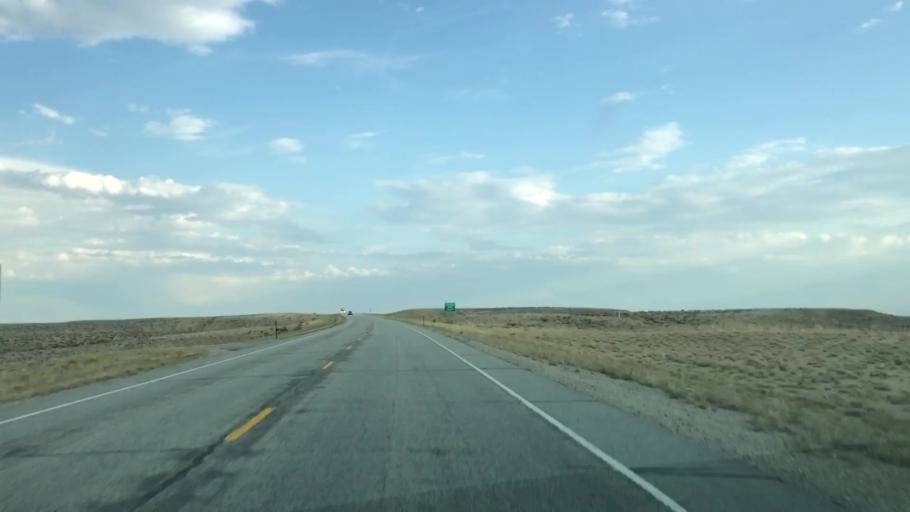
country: US
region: Wyoming
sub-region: Sweetwater County
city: North Rock Springs
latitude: 42.2807
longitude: -109.4856
